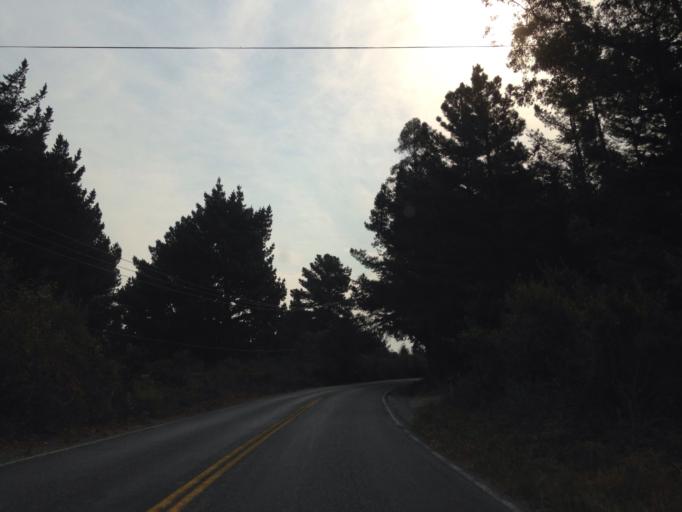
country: US
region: California
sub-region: San Mateo County
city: Highlands-Baywood Park
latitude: 37.4697
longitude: -122.3522
